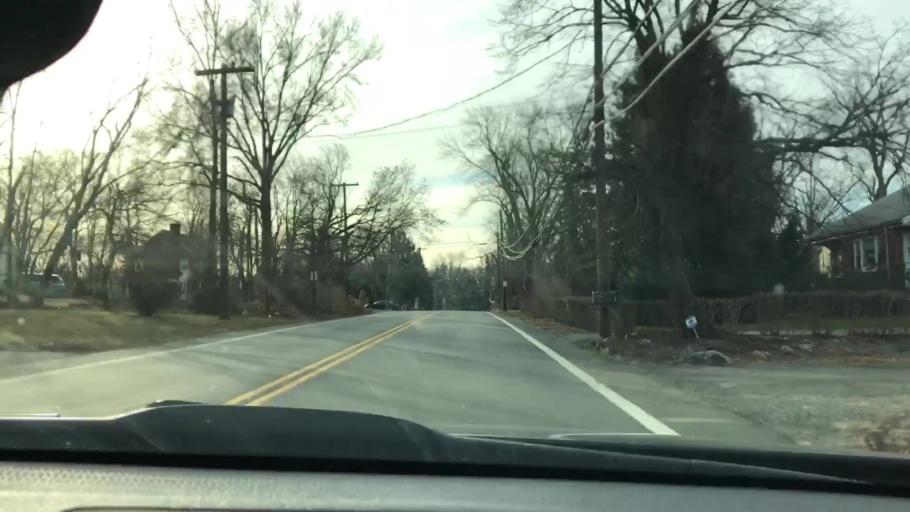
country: US
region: New Jersey
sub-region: Morris County
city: Parsippany
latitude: 40.8403
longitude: -74.4220
